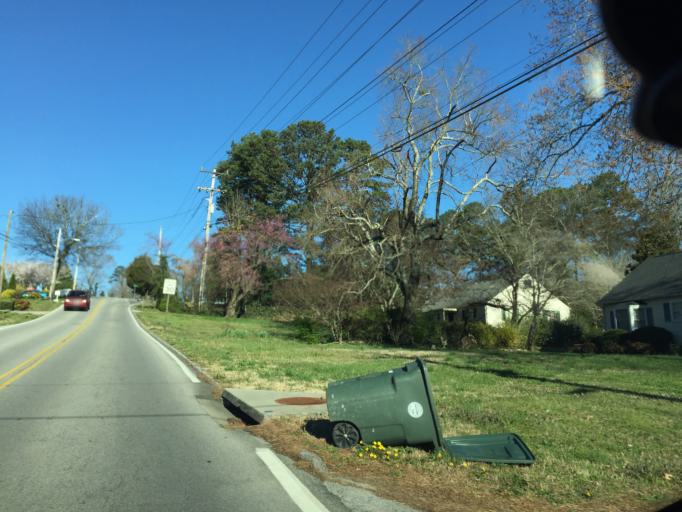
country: US
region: Tennessee
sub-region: Hamilton County
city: East Brainerd
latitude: 35.0290
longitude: -85.1631
